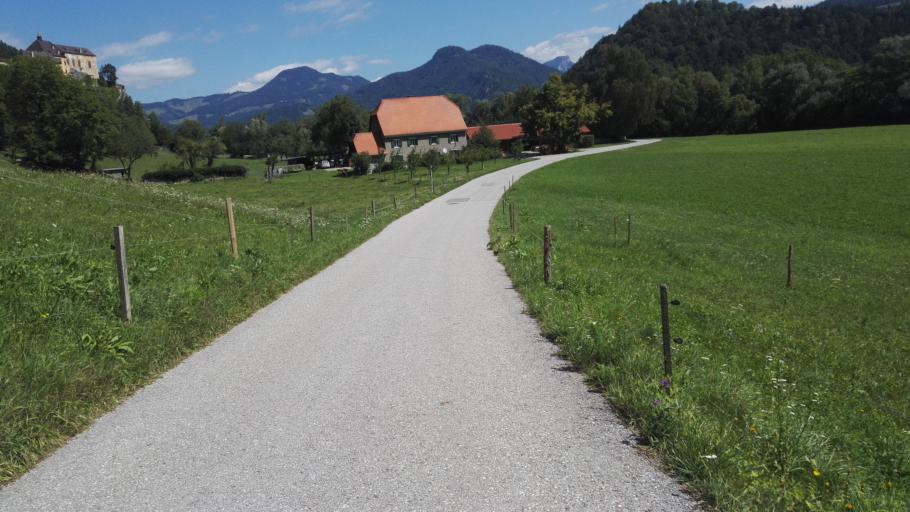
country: AT
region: Styria
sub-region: Politischer Bezirk Graz-Umgebung
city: Frohnleiten
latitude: 47.2423
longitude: 15.3096
